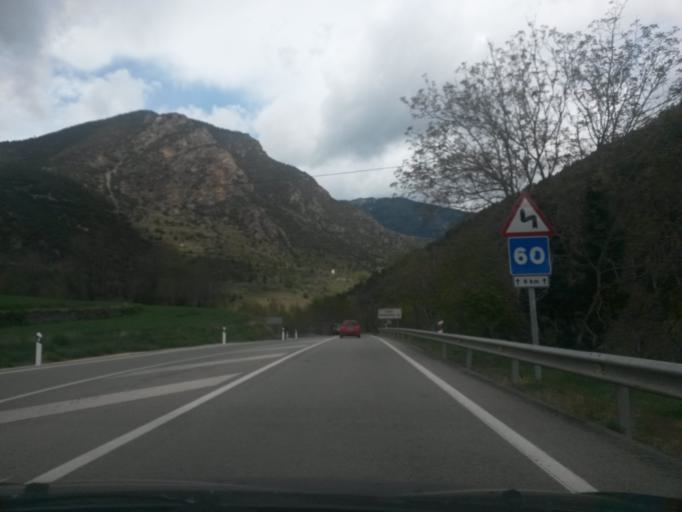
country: ES
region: Catalonia
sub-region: Provincia de Lleida
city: el Pont de Bar
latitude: 42.3620
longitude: 1.5875
